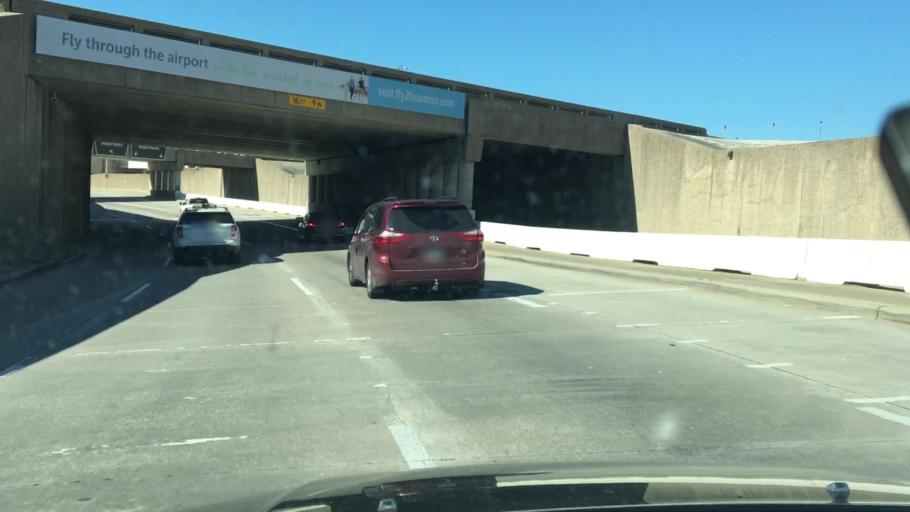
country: US
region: Texas
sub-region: Harris County
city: Humble
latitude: 29.9870
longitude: -95.3298
